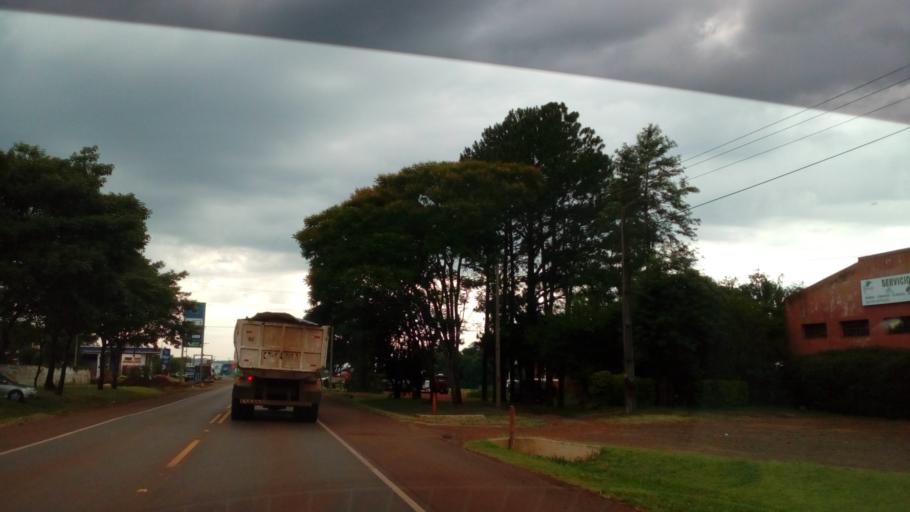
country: PY
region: Itapua
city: Obligado
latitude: -27.0732
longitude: -55.6213
